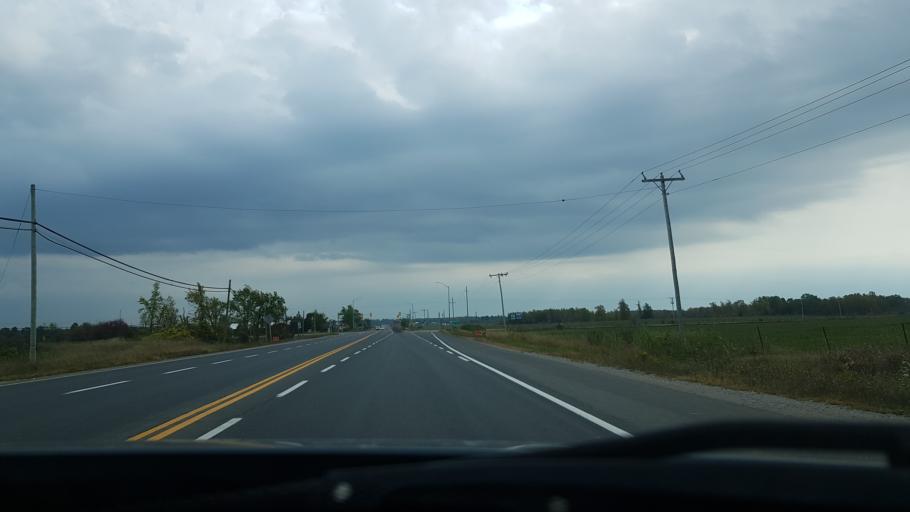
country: CA
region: Ontario
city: Omemee
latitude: 44.3769
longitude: -78.7809
